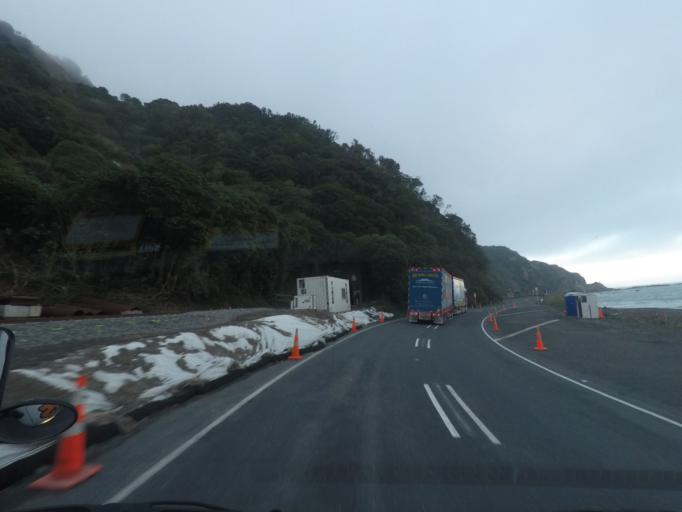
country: NZ
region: Canterbury
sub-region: Kaikoura District
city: Kaikoura
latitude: -42.4521
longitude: 173.5674
